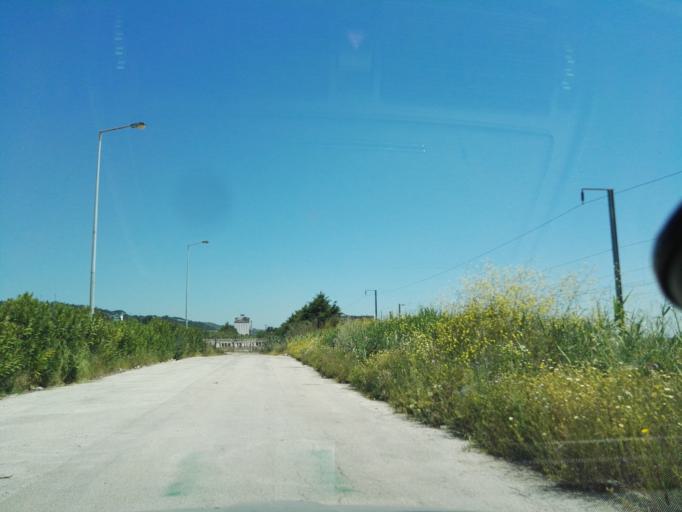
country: PT
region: Lisbon
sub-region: Vila Franca de Xira
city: Sobralinho
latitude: 38.9063
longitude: -9.0209
